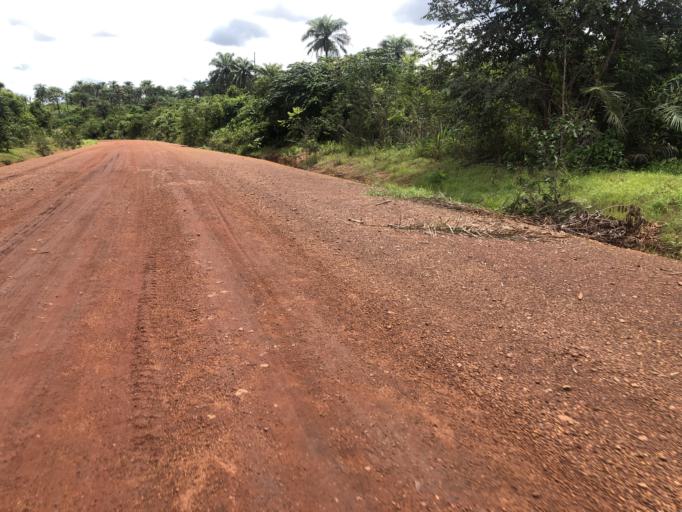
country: SL
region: Northern Province
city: Port Loko
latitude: 8.7164
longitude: -12.8361
